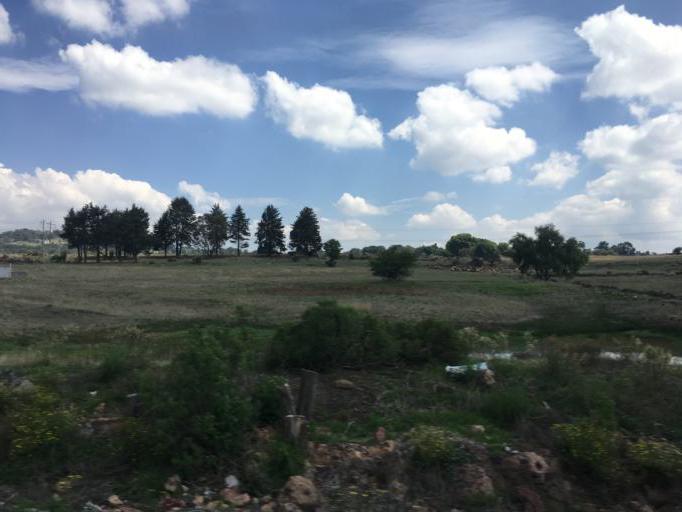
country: MX
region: Mexico
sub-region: Jilotepec
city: Octeyuco Dos Mil
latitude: 19.8877
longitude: -99.6426
